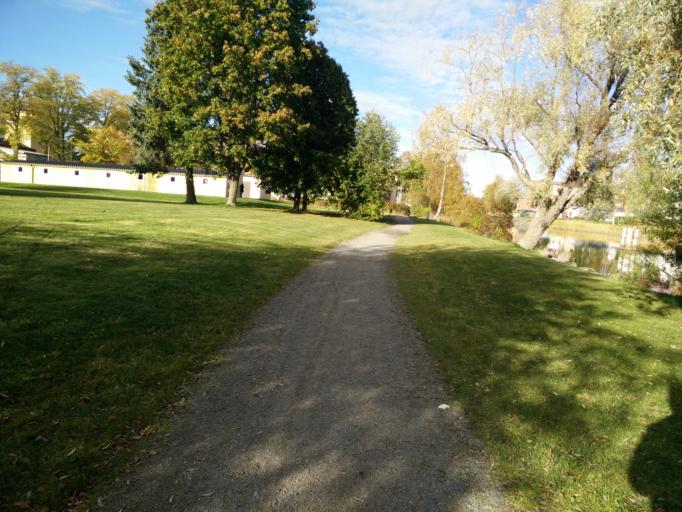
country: SE
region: Vaesternorrland
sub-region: Haernoesands Kommun
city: Haernoesand
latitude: 62.6275
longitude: 17.9362
